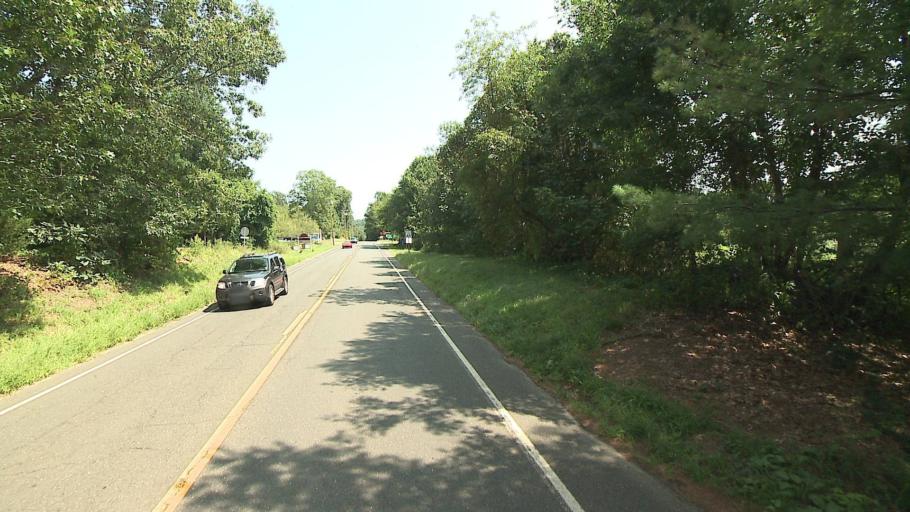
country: US
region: Connecticut
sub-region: Fairfield County
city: Shelton
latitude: 41.3347
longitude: -73.1791
